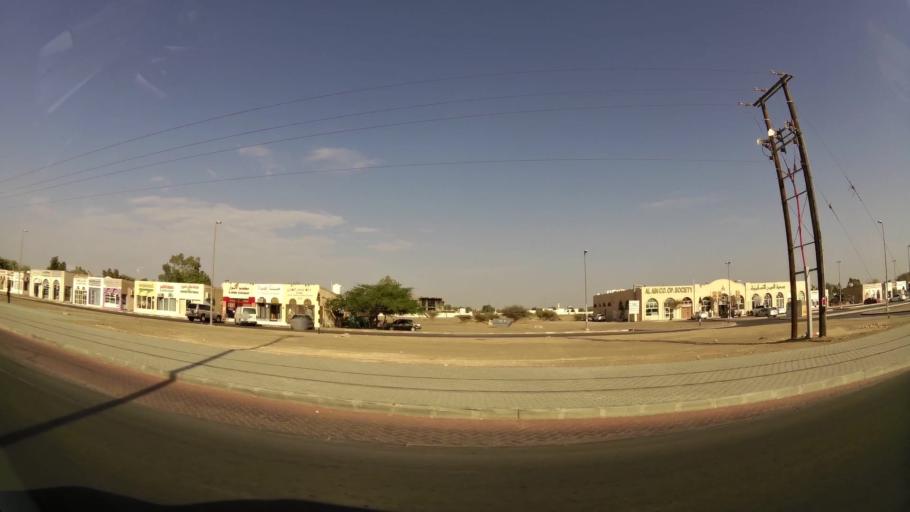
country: AE
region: Abu Dhabi
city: Al Ain
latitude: 24.0403
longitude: 55.8436
